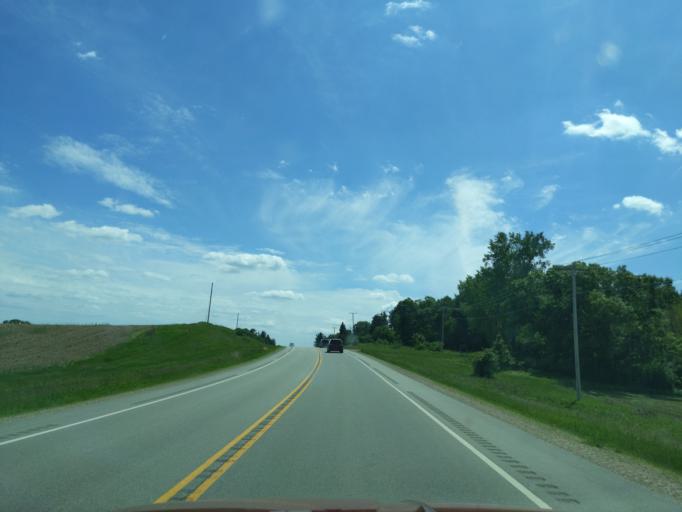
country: US
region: Wisconsin
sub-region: Columbia County
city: Pardeeville
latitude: 43.4601
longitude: -89.3239
